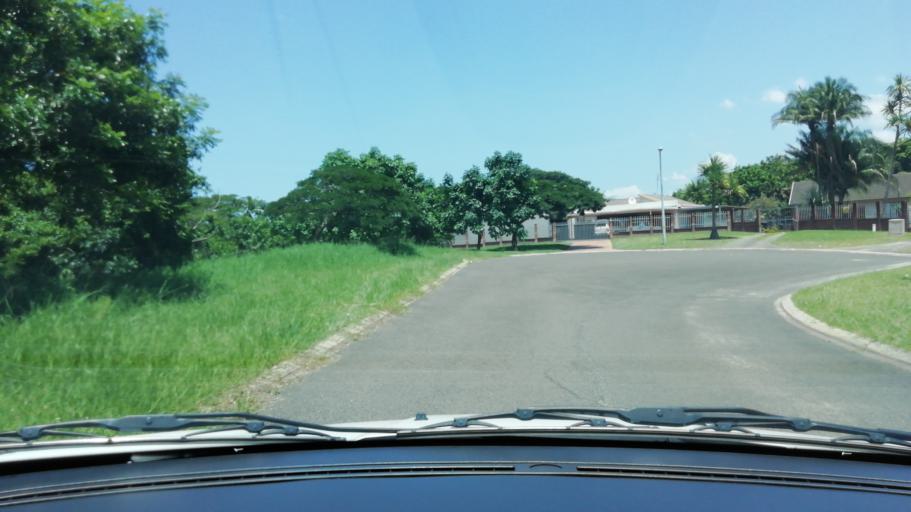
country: ZA
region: KwaZulu-Natal
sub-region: uThungulu District Municipality
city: Richards Bay
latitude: -28.7365
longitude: 32.0596
